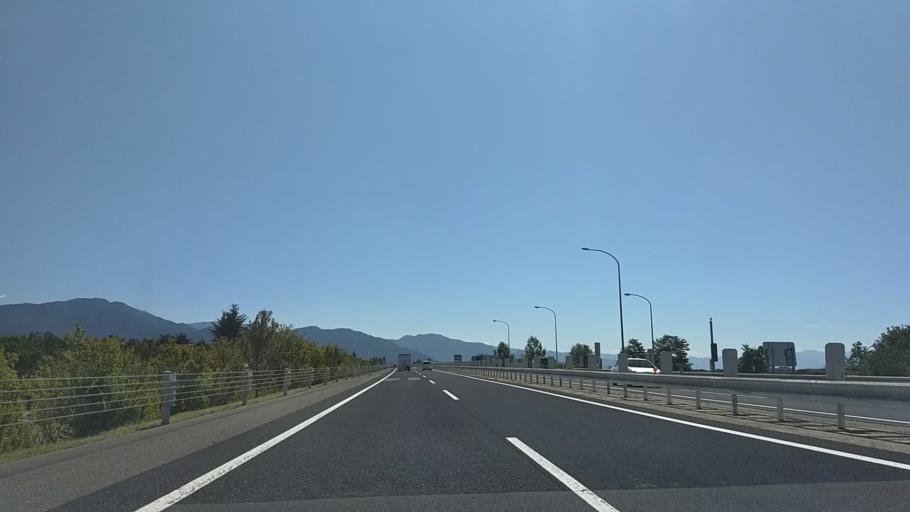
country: JP
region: Nagano
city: Suzaka
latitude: 36.6904
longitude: 138.2936
